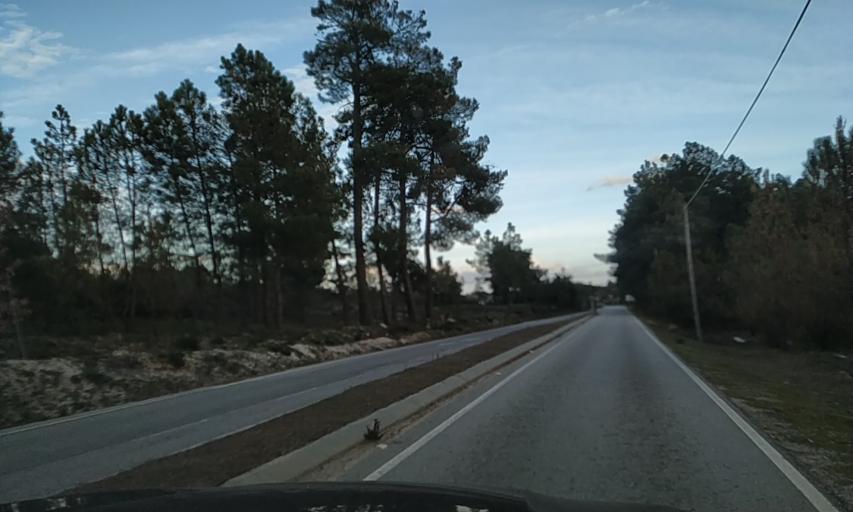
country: PT
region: Braganca
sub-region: Carrazeda de Ansiaes
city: Carrazeda de Anciaes
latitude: 41.2471
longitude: -7.3230
